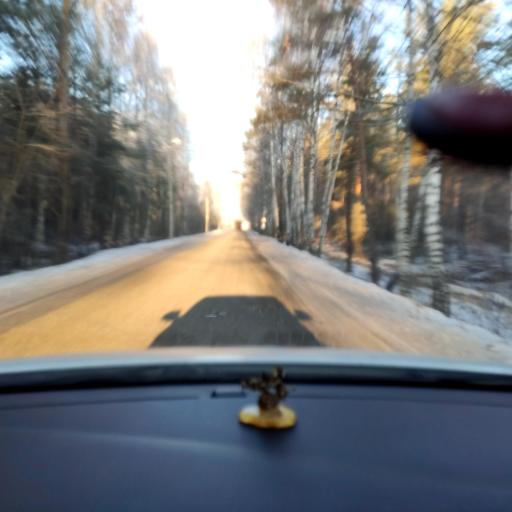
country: RU
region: Tatarstan
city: Stolbishchi
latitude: 55.6730
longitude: 49.1201
